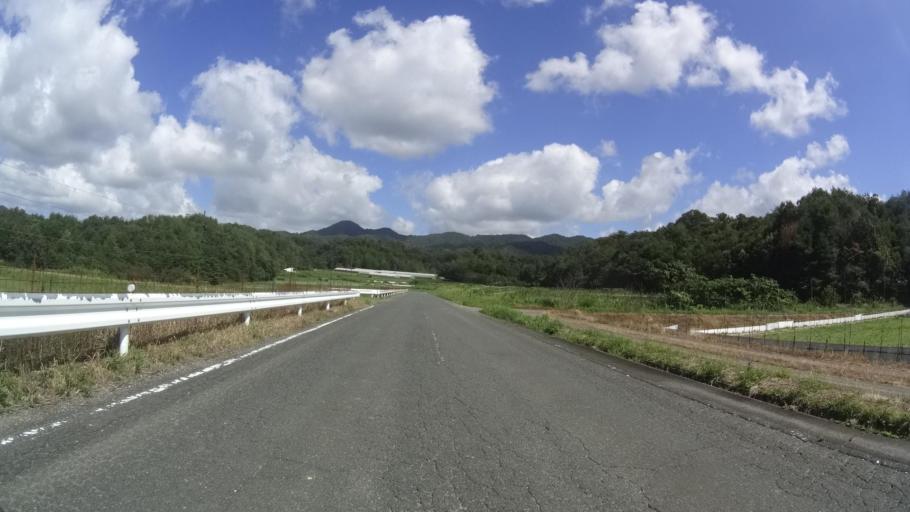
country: JP
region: Kyoto
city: Miyazu
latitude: 35.6726
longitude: 135.1061
